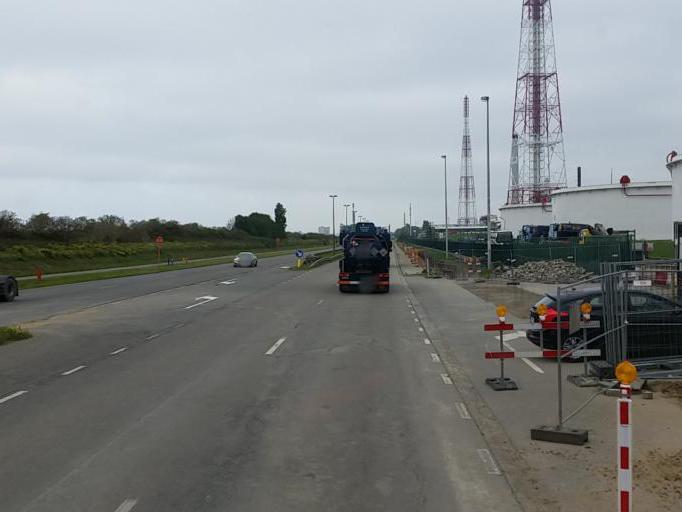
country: BE
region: Flanders
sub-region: Provincie Antwerpen
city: Zwijndrecht
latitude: 51.2671
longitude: 4.3125
